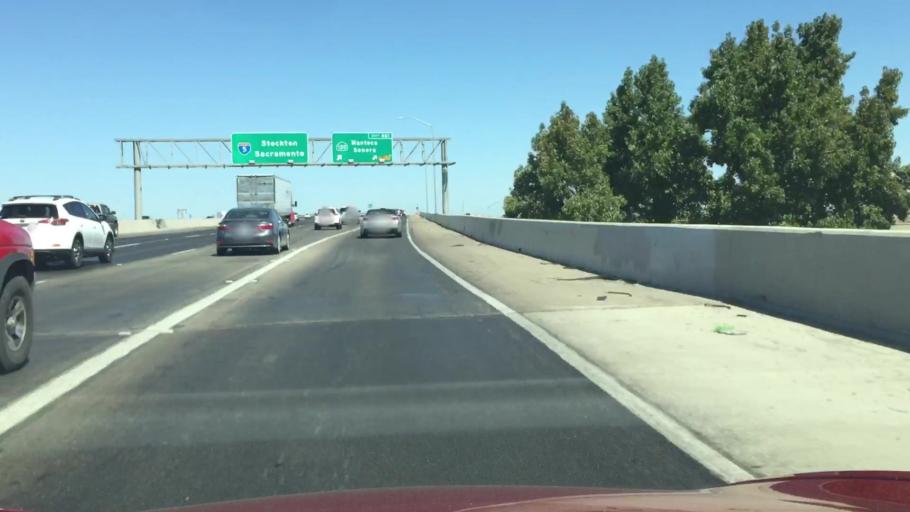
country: US
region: California
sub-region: San Joaquin County
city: Lathrop
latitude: 37.7845
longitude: -121.3062
